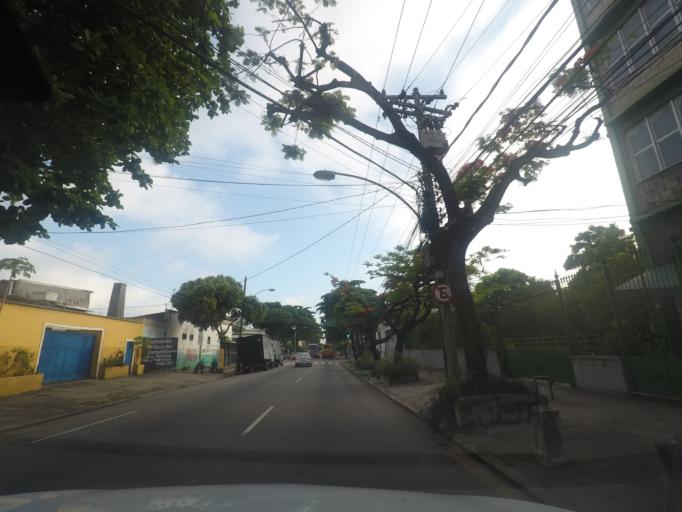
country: BR
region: Rio de Janeiro
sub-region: Duque De Caxias
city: Duque de Caxias
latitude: -22.8334
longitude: -43.2768
